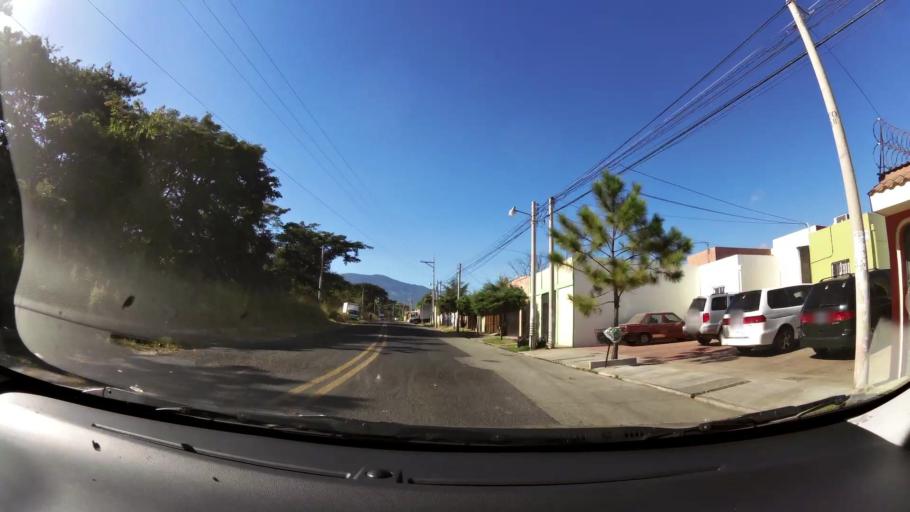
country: SV
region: Santa Ana
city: Santa Ana
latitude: 13.9622
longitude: -89.5759
